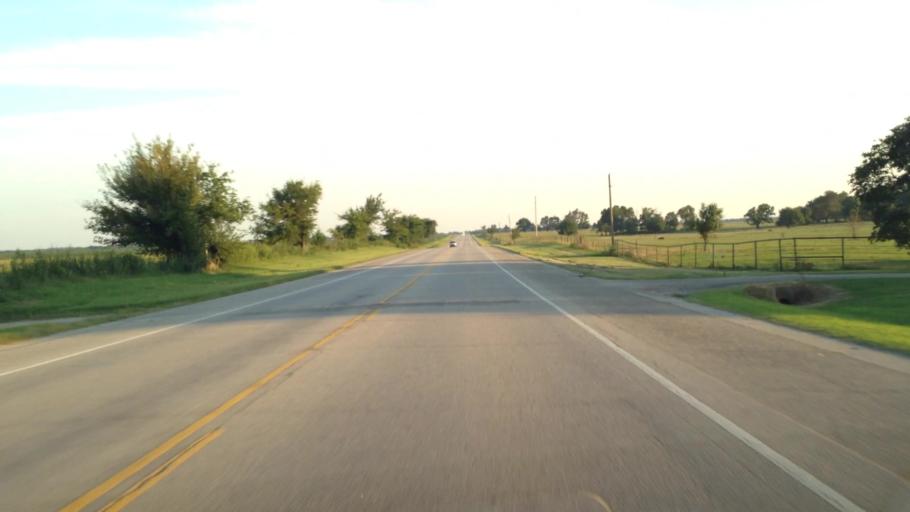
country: US
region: Oklahoma
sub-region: Ottawa County
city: Afton
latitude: 36.6541
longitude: -94.9815
